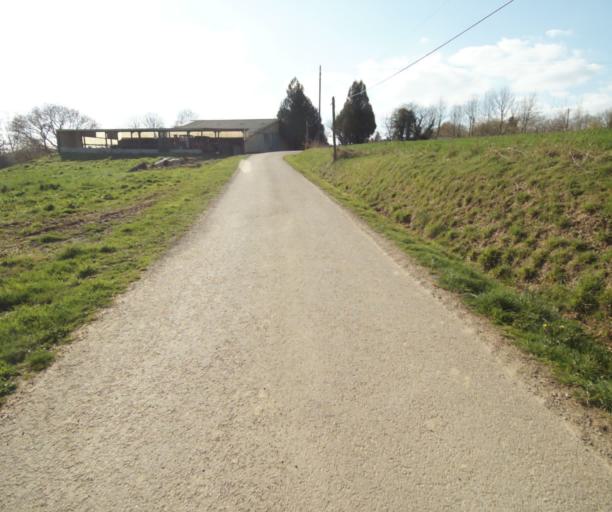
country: FR
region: Limousin
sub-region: Departement de la Correze
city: Saint-Mexant
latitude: 45.3312
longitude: 1.6113
